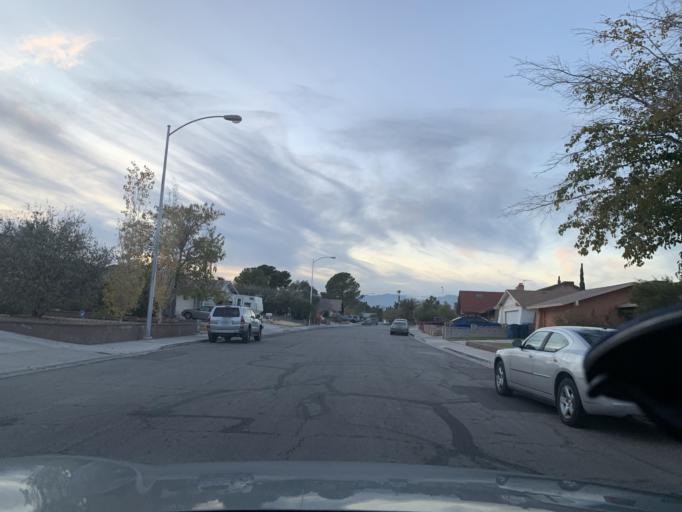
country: US
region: Nevada
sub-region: Clark County
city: Spring Valley
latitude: 36.0944
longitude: -115.2288
